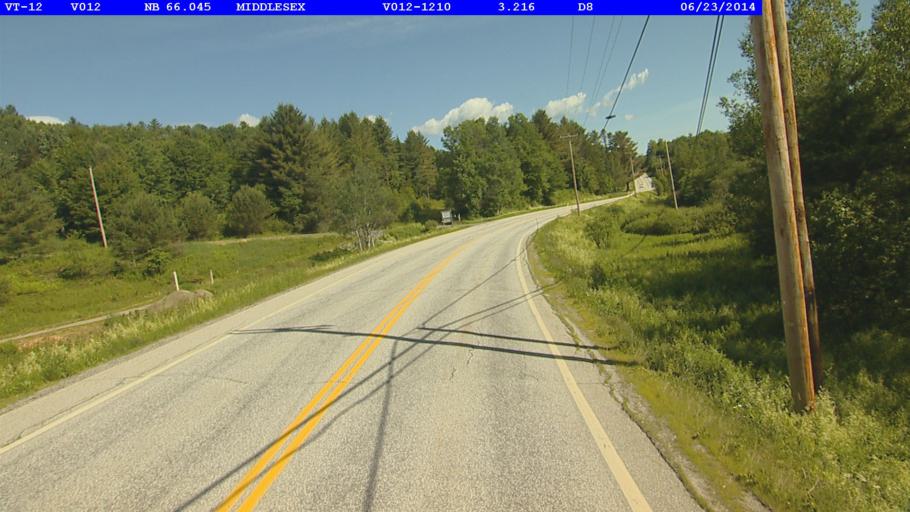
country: US
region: Vermont
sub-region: Washington County
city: Montpelier
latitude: 44.3466
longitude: -72.5659
